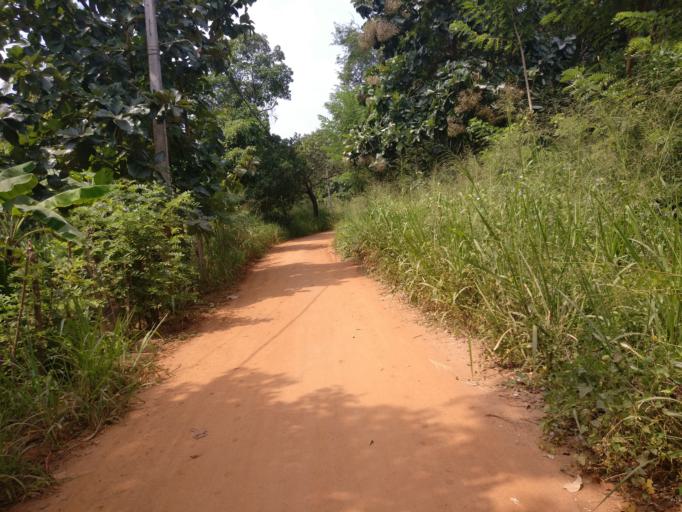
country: LK
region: Central
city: Dambulla
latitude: 7.8406
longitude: 80.6488
